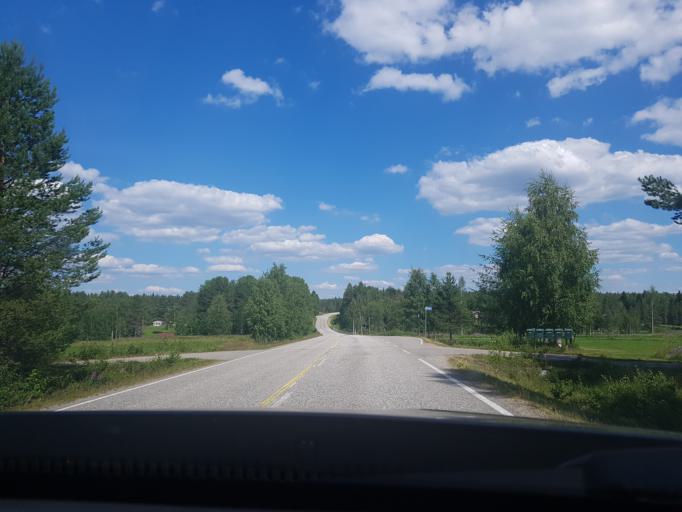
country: FI
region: Kainuu
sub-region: Kehys-Kainuu
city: Kuhmo
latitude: 64.1997
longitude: 29.6916
